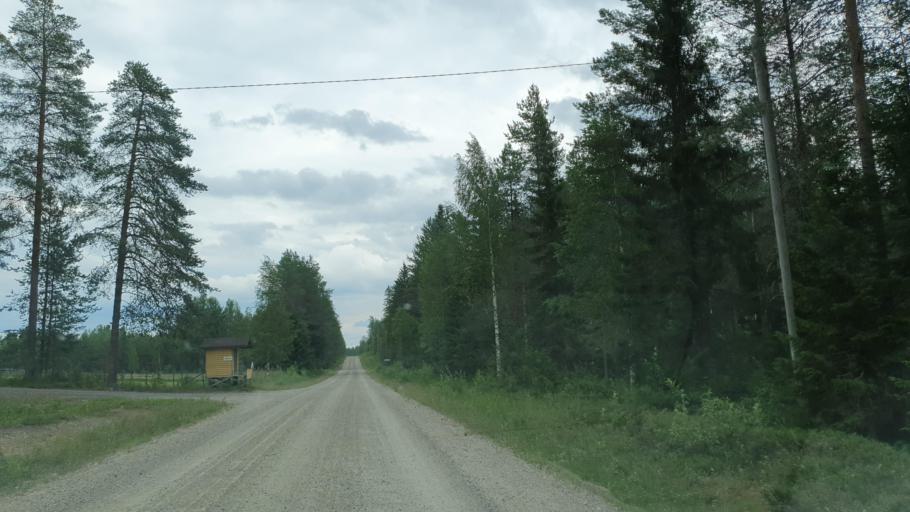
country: RU
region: Republic of Karelia
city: Kostomuksha
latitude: 64.7525
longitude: 29.8968
